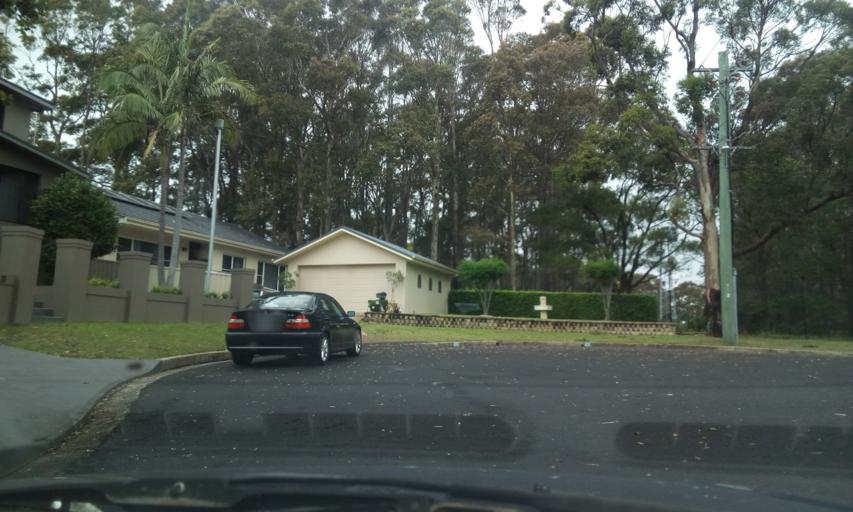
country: AU
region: New South Wales
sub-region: Wollongong
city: Mangerton
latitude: -34.4367
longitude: 150.8746
